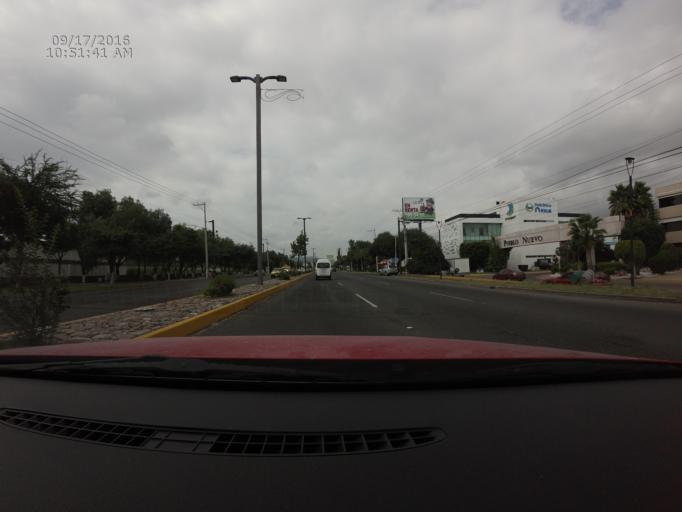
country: MX
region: Queretaro
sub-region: Corregidora
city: El Pueblito
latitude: 20.5462
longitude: -100.4277
